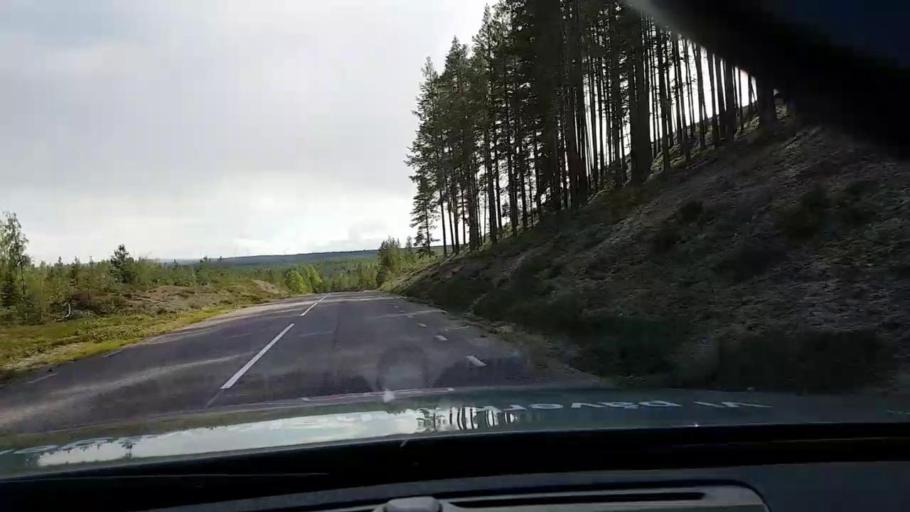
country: SE
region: Vaesterbotten
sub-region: Asele Kommun
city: Asele
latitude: 63.8739
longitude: 17.3568
